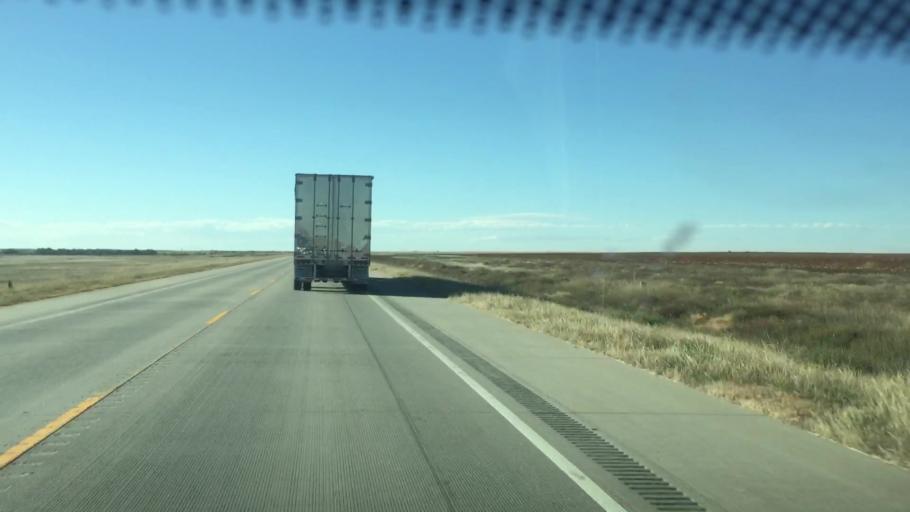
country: US
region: Colorado
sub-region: Kiowa County
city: Eads
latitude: 38.7982
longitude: -102.9515
